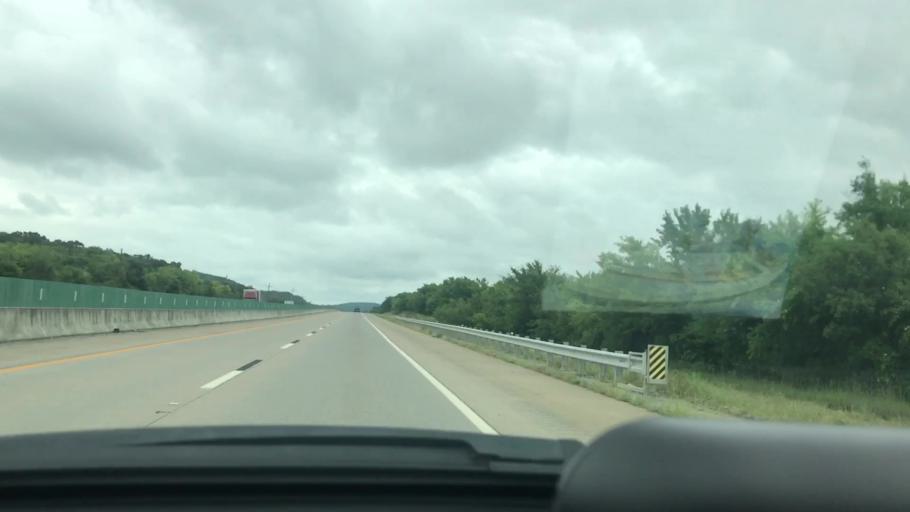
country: US
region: Oklahoma
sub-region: Pittsburg County
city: Krebs
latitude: 35.0715
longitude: -95.7046
